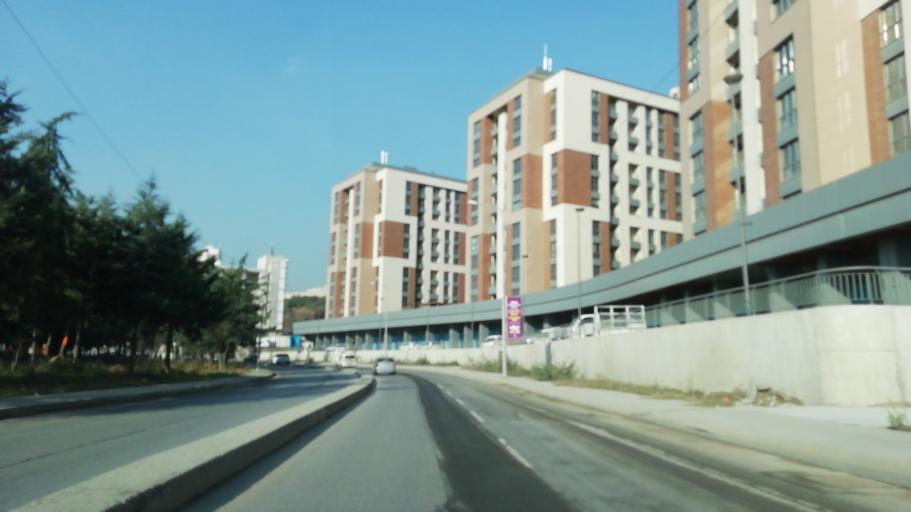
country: TR
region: Istanbul
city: Sisli
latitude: 41.0874
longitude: 28.9493
